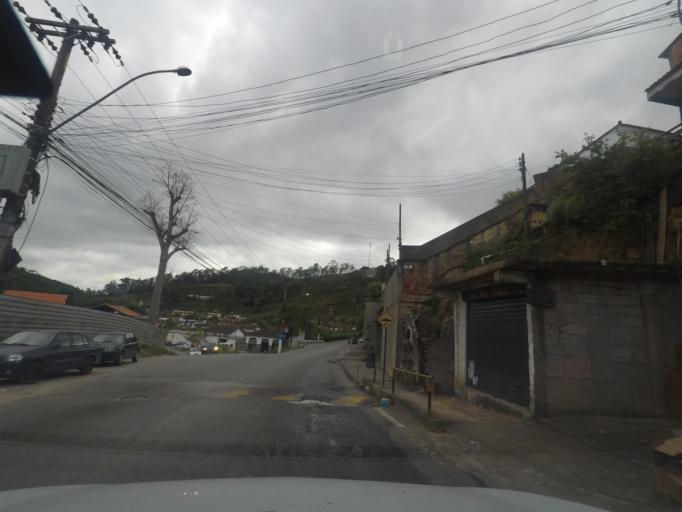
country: BR
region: Rio de Janeiro
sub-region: Teresopolis
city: Teresopolis
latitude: -22.3876
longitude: -42.9561
